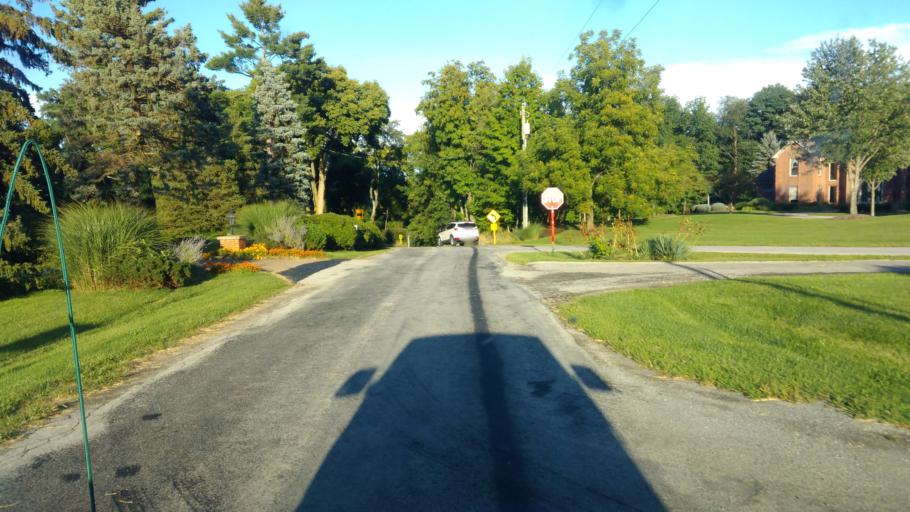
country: US
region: Ohio
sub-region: Wyandot County
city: Upper Sandusky
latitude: 40.8619
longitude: -83.2562
